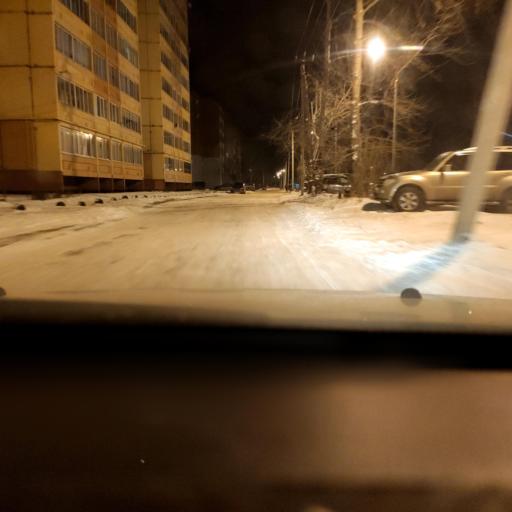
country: RU
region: Perm
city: Polazna
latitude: 58.1257
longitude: 56.3894
